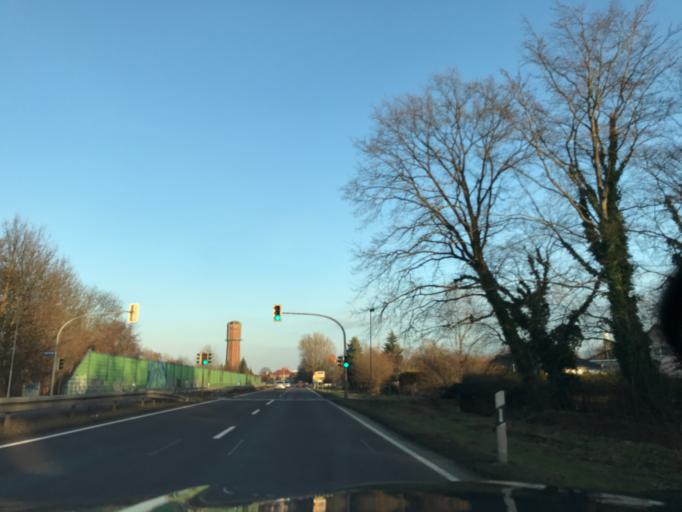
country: DE
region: Saxony-Anhalt
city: Genthin
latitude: 52.4071
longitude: 12.1484
